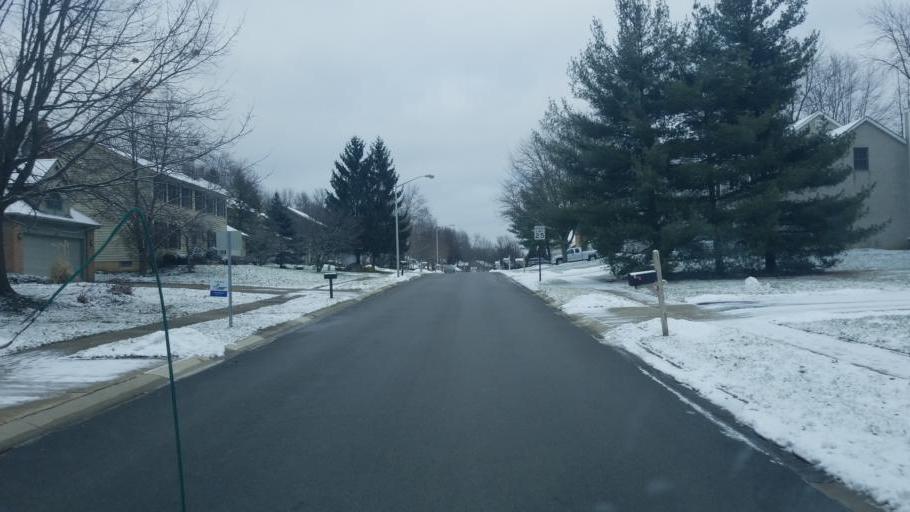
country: US
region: Ohio
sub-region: Franklin County
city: Gahanna
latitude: 40.0487
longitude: -82.8518
